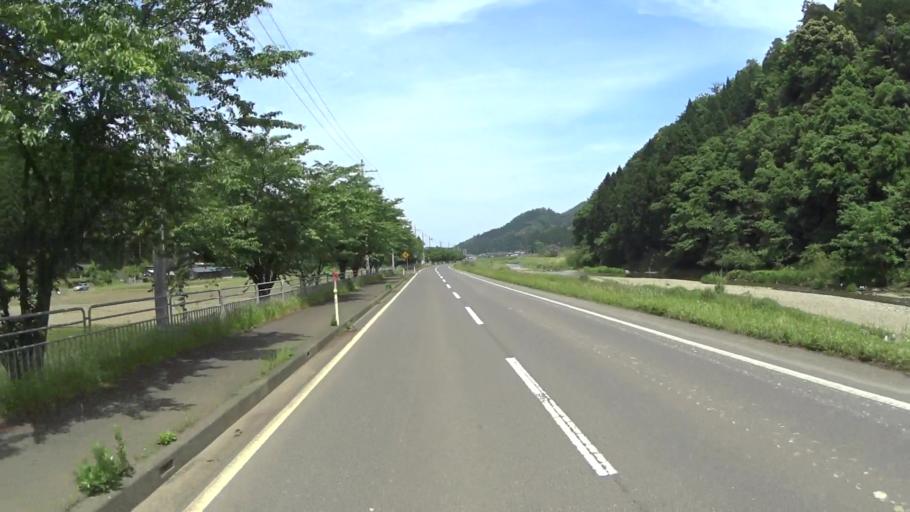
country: JP
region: Kyoto
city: Maizuru
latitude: 35.4398
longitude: 135.5381
